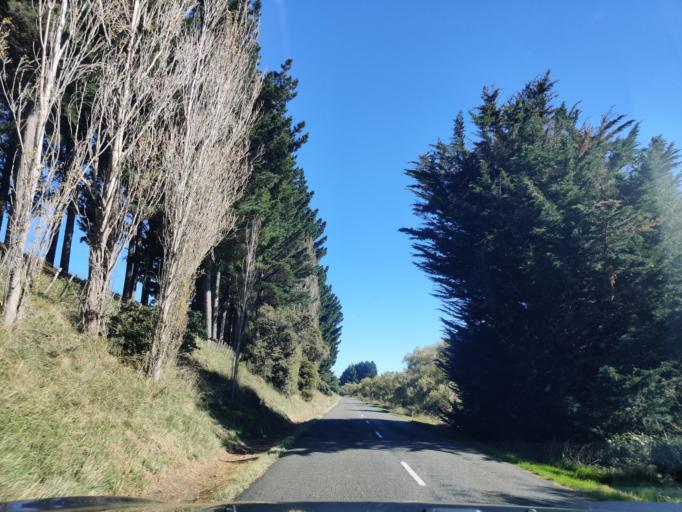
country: NZ
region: Manawatu-Wanganui
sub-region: Palmerston North City
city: Palmerston North
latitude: -40.2577
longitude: 175.7039
